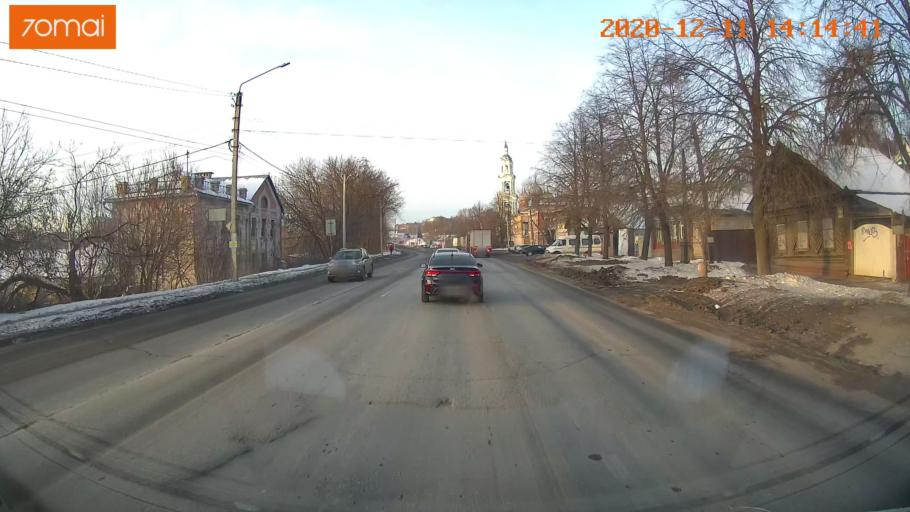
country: RU
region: Kostroma
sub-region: Kostromskoy Rayon
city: Kostroma
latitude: 57.7535
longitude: 40.9503
